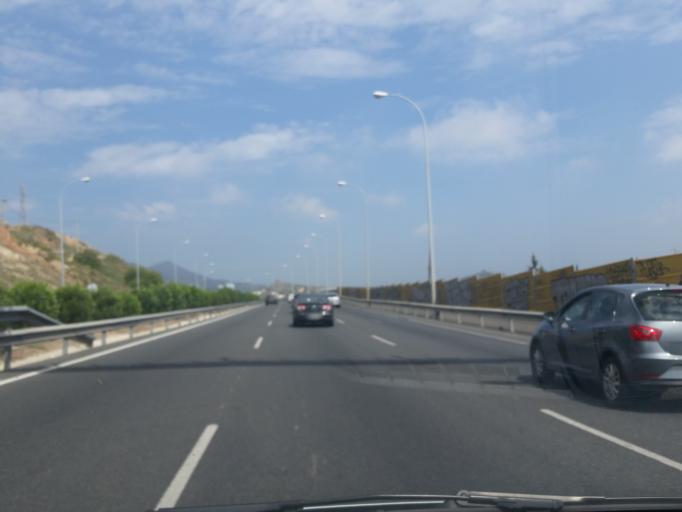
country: ES
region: Andalusia
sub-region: Provincia de Malaga
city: Malaga
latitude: 36.7316
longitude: -4.4541
